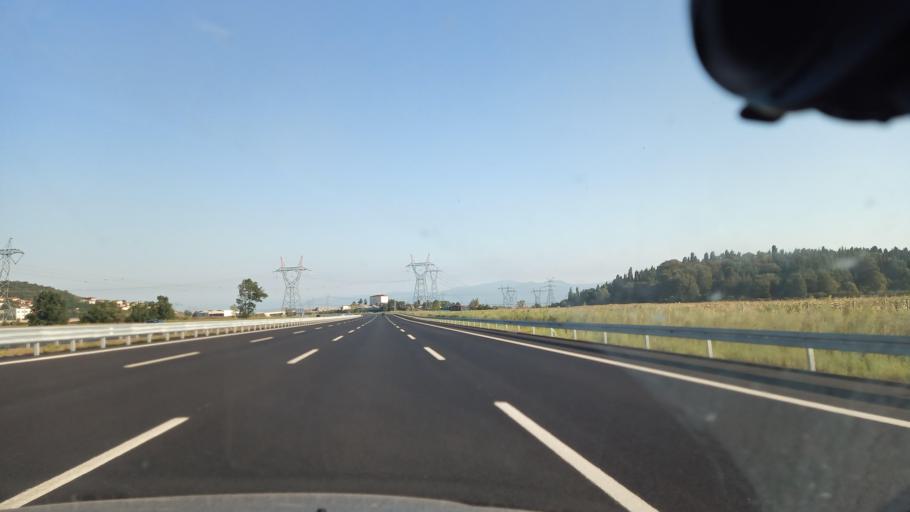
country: TR
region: Sakarya
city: Adapazari
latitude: 40.8325
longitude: 30.3881
